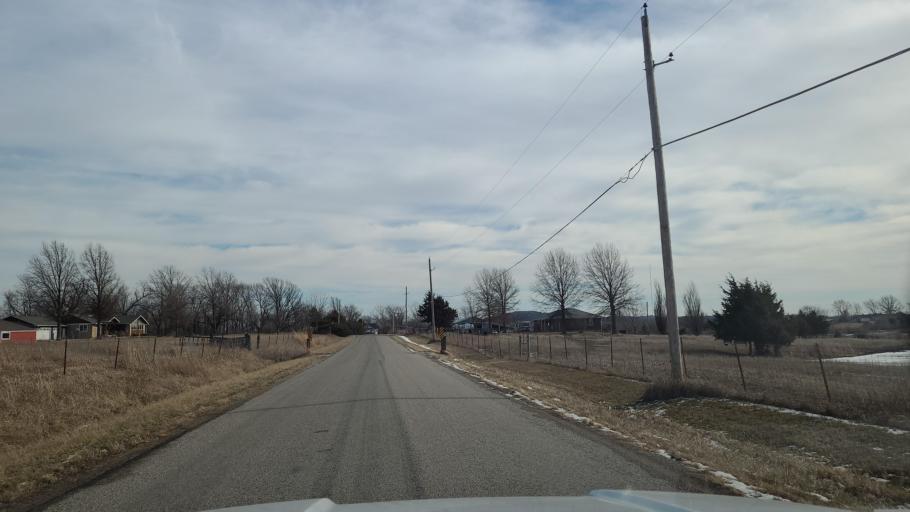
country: US
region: Kansas
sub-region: Douglas County
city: Lawrence
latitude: 38.9108
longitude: -95.2187
